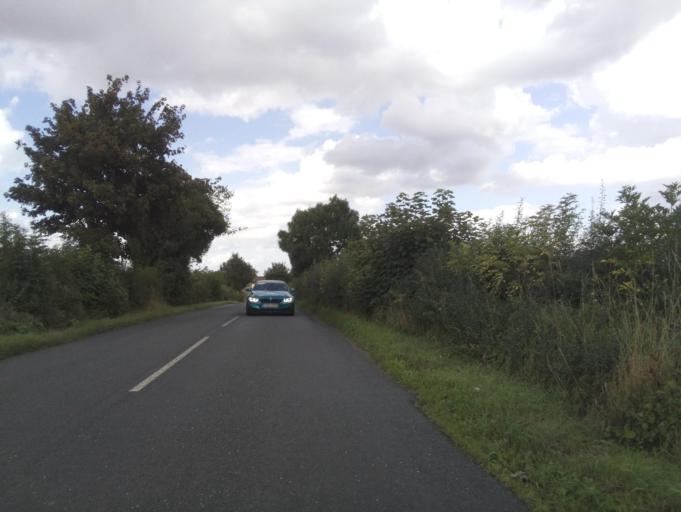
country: GB
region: England
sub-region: North Yorkshire
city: Bedale
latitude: 54.2453
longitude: -1.6909
